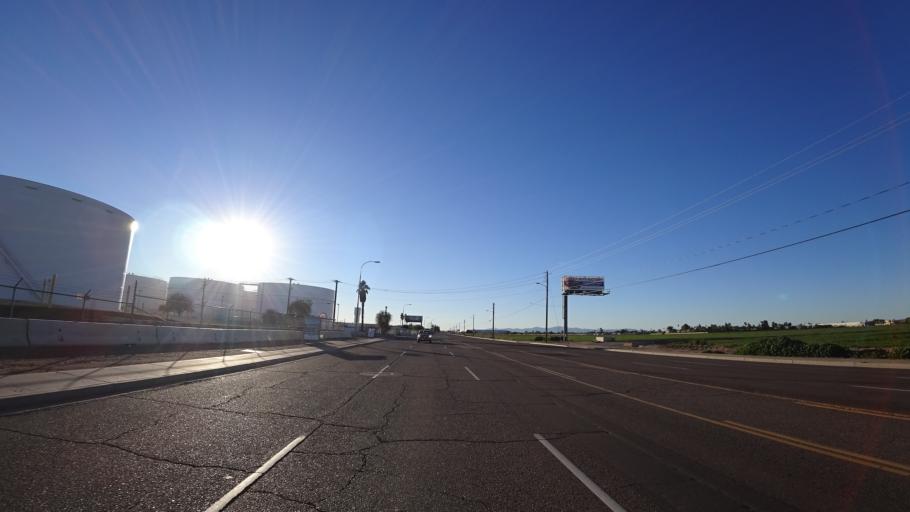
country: US
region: Arizona
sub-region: Maricopa County
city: Tolleson
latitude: 33.4512
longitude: -112.1769
